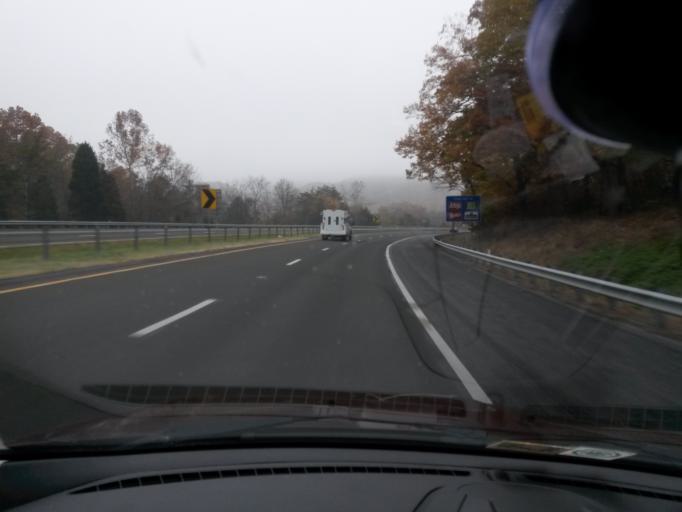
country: US
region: Virginia
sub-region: City of Covington
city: Fairlawn
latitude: 37.7718
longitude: -79.9828
